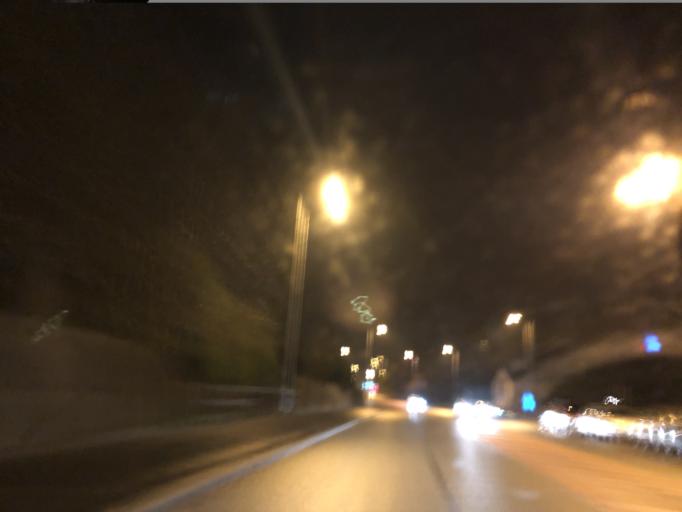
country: GB
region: England
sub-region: Borough of Oldham
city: Shaw
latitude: 53.5570
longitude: -2.0818
